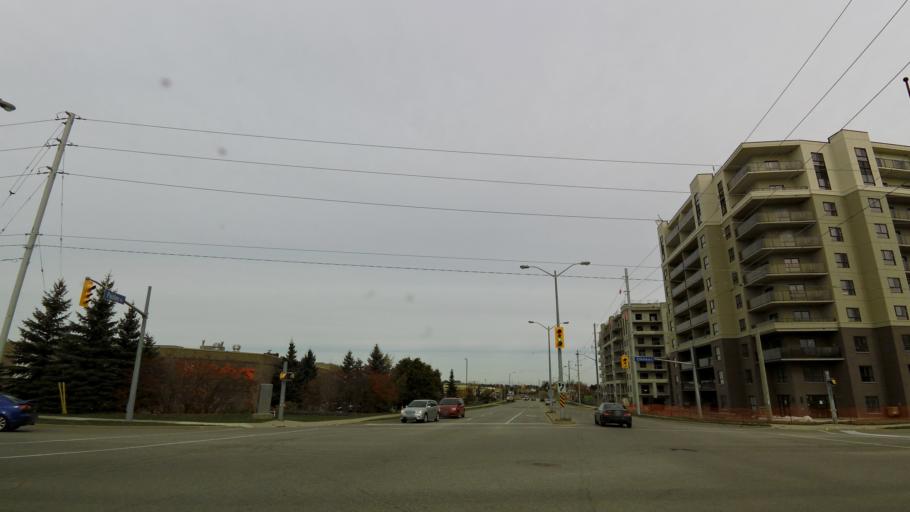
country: CA
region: Ontario
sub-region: Wellington County
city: Guelph
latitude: 43.5216
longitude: -80.2891
